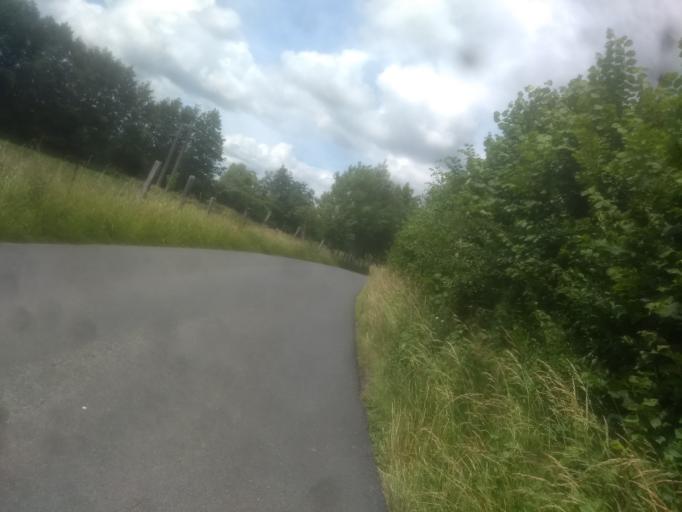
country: FR
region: Nord-Pas-de-Calais
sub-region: Departement du Pas-de-Calais
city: Maroeuil
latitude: 50.3314
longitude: 2.6891
